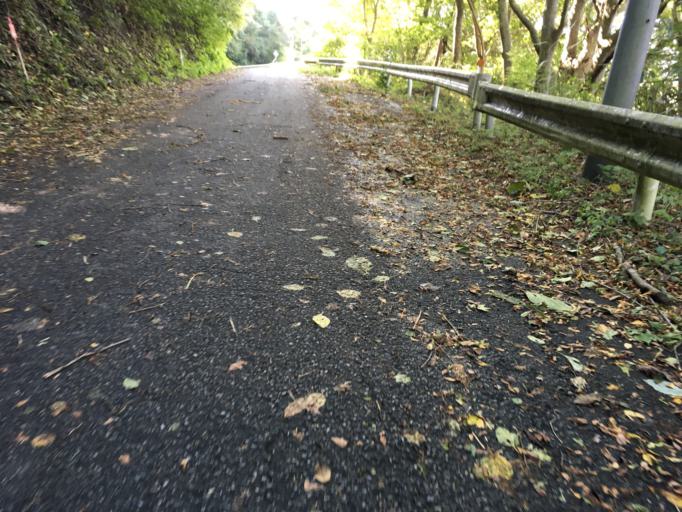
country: JP
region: Iwate
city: Ichinoseki
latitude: 38.8297
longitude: 141.2599
